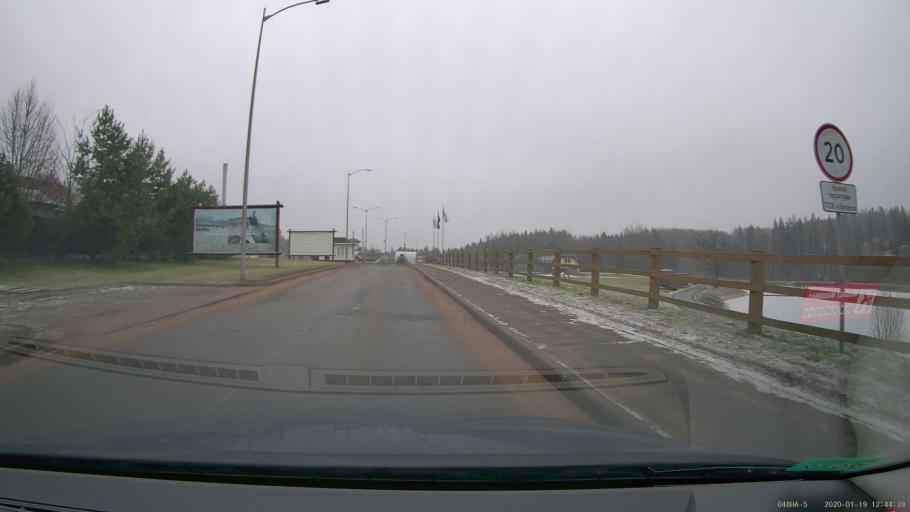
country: BY
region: Minsk
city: Lahoysk
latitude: 54.1808
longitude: 27.8070
